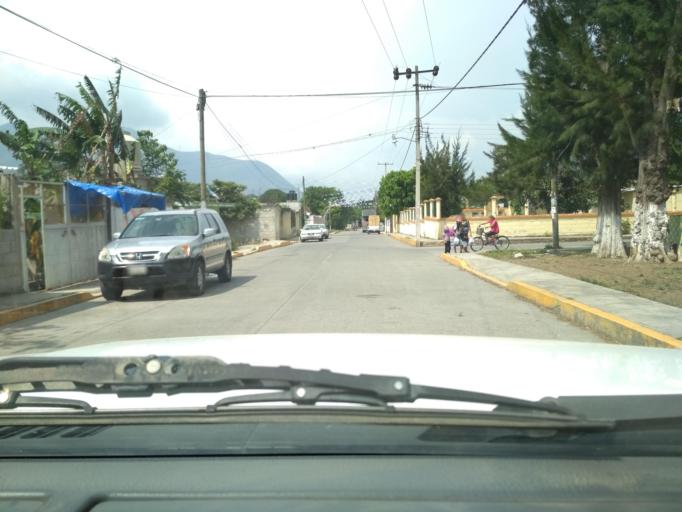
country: MX
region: Veracruz
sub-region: Acultzingo
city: Acatla
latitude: 18.7656
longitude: -97.2194
